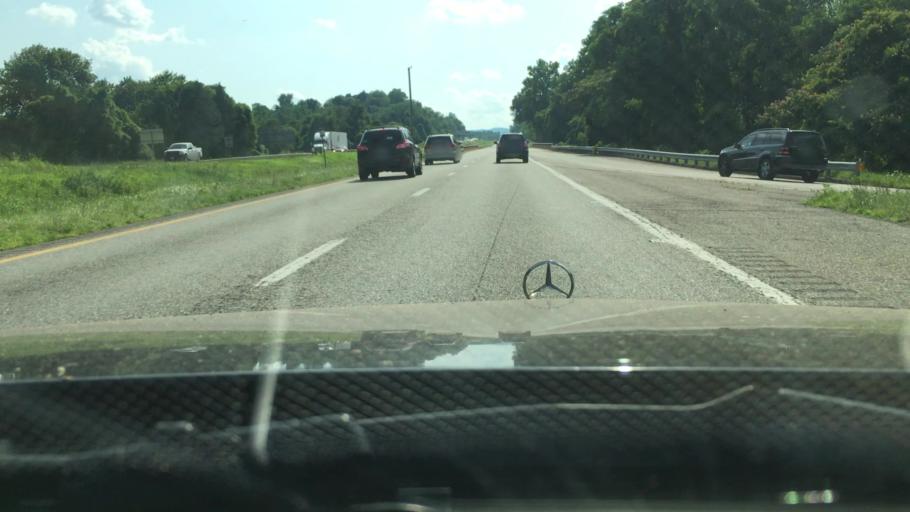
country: US
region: Virginia
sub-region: City of Charlottesville
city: Charlottesville
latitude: 38.0118
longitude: -78.4747
